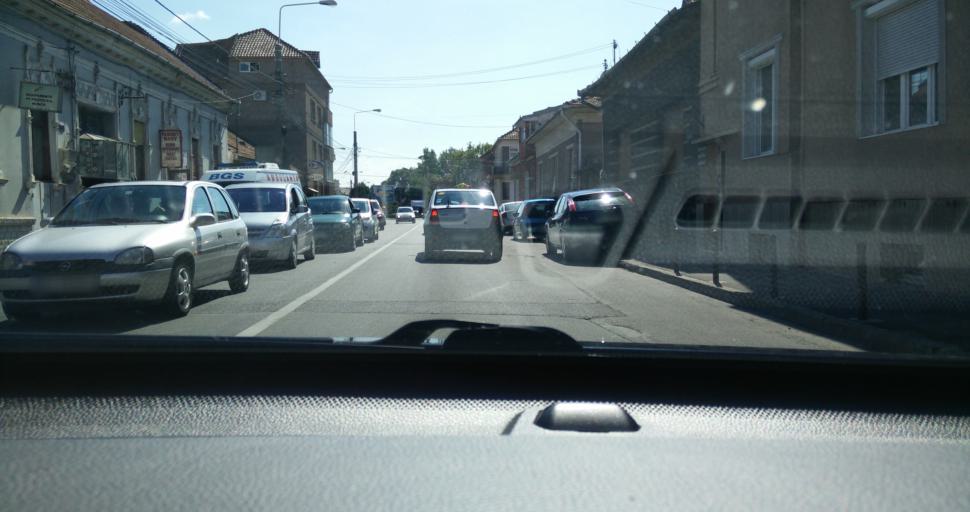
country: RO
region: Bihor
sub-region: Comuna Biharea
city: Oradea
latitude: 47.0500
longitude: 21.9269
